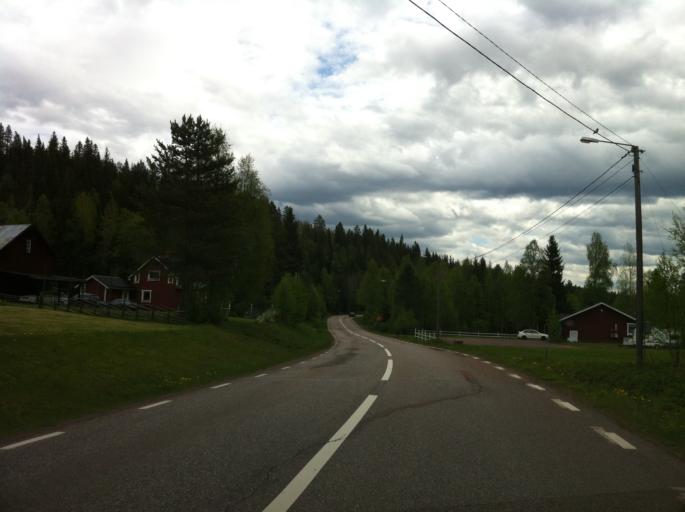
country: SE
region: Dalarna
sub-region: Malung-Saelens kommun
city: Malung
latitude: 61.2247
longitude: 13.2190
